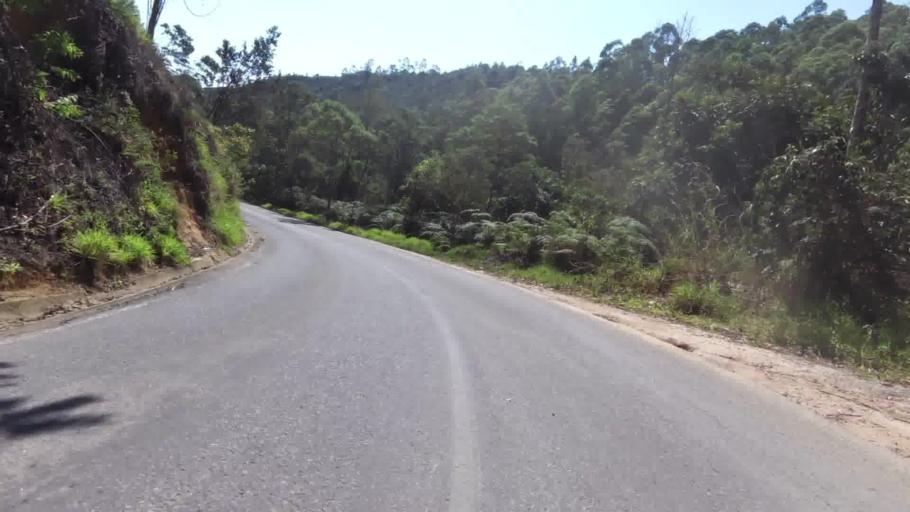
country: BR
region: Espirito Santo
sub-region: Marechal Floriano
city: Marechal Floriano
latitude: -20.4587
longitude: -40.9041
